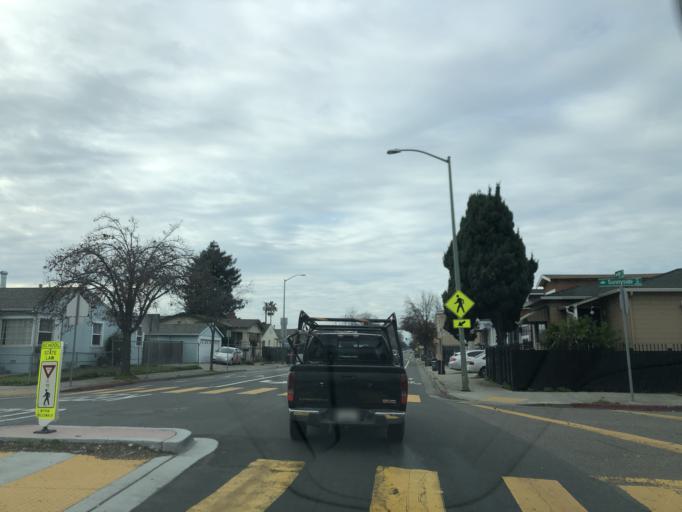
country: US
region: California
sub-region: Alameda County
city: San Leandro
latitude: 37.7481
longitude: -122.1628
